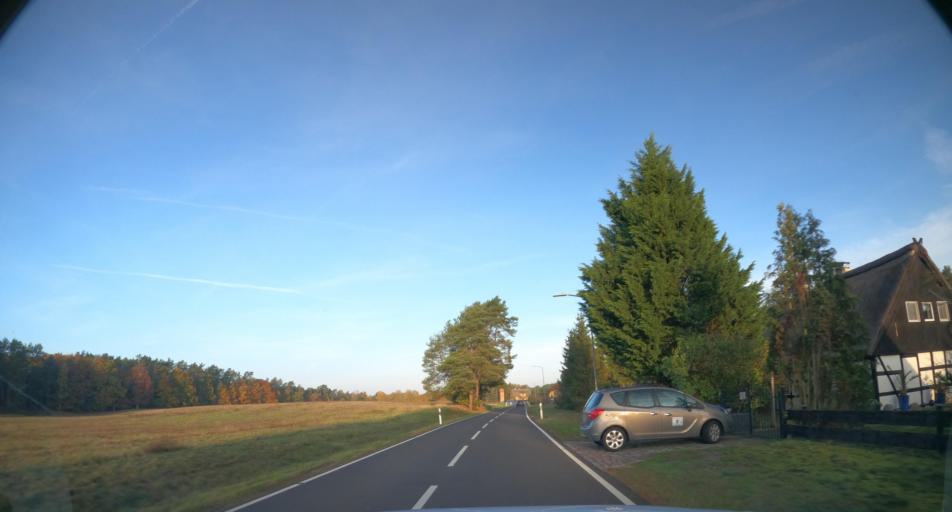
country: DE
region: Mecklenburg-Vorpommern
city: Ahlbeck
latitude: 53.6369
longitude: 14.2166
